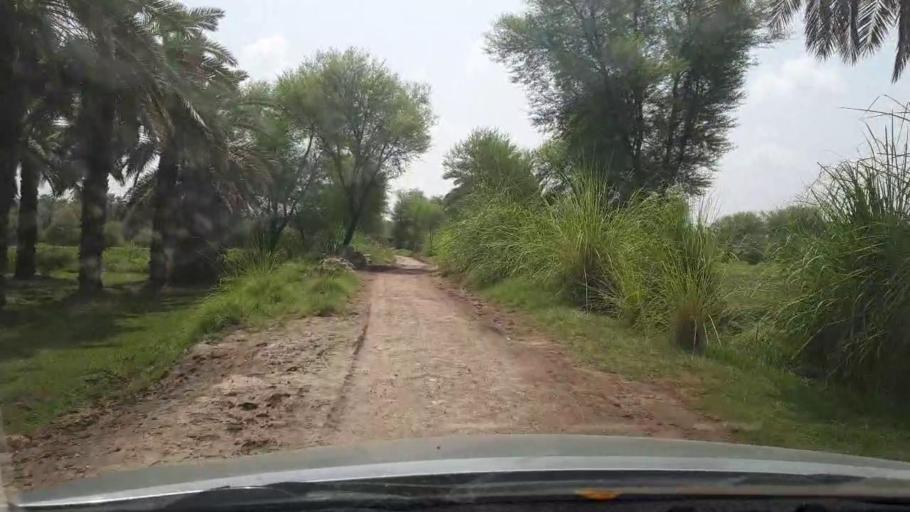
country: PK
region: Sindh
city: Khairpur
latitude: 27.4846
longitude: 68.7317
